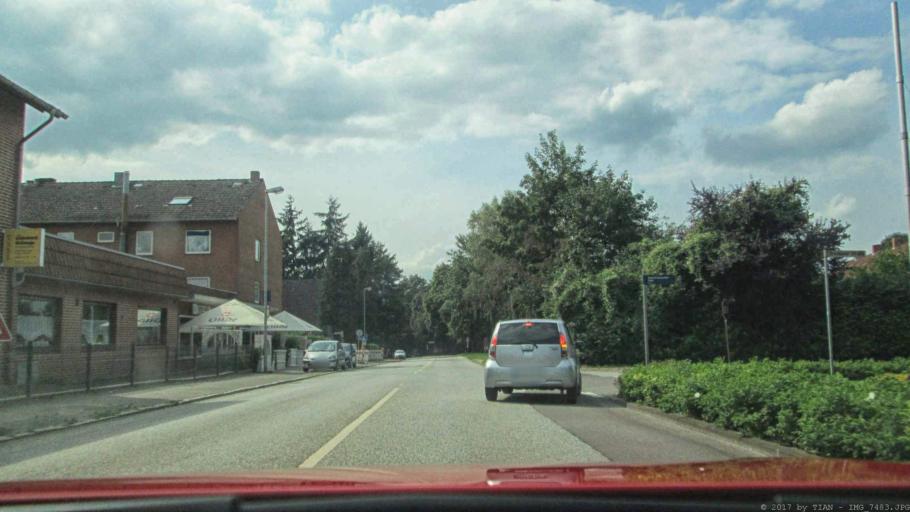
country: DE
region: Schleswig-Holstein
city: Lauenburg
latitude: 53.3740
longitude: 10.5422
